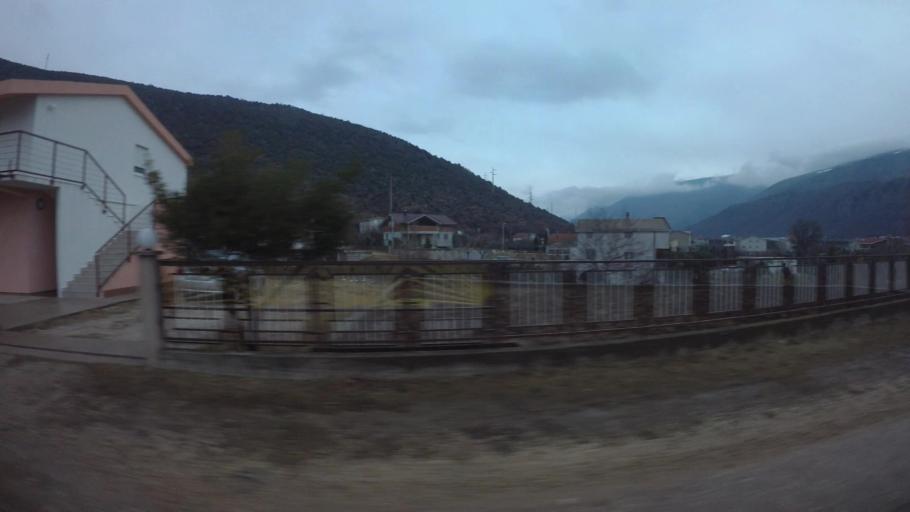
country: BA
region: Federation of Bosnia and Herzegovina
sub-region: Hercegovacko-Bosanski Kanton
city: Mostar
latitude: 43.3677
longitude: 17.8123
